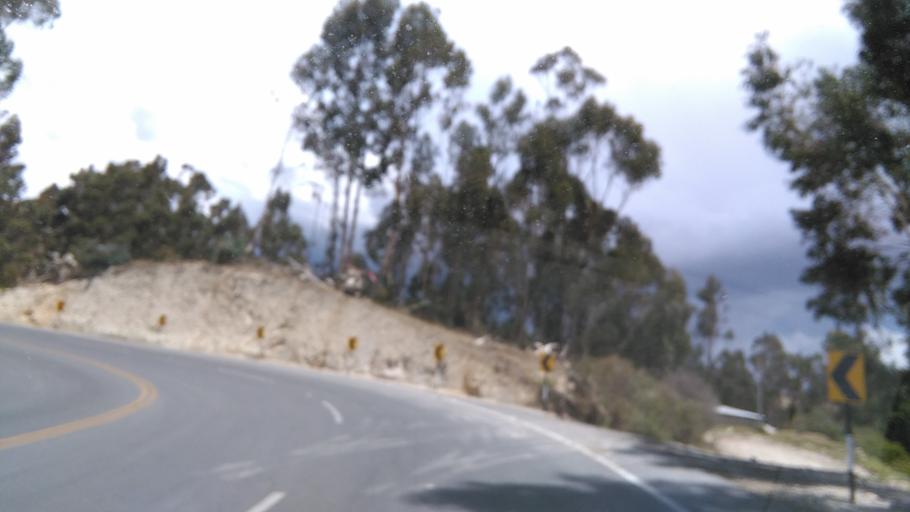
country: PE
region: Apurimac
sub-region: Provincia de Andahuaylas
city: San Jeronimo
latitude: -13.6857
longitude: -73.3579
